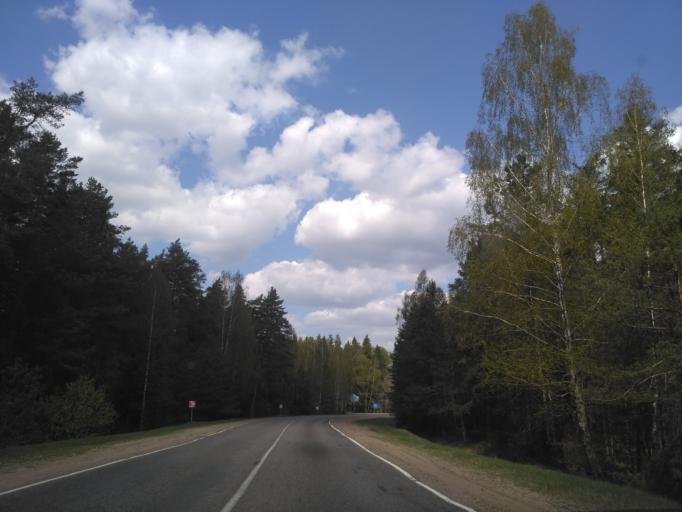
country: BY
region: Minsk
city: Il'ya
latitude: 54.4923
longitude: 27.2370
